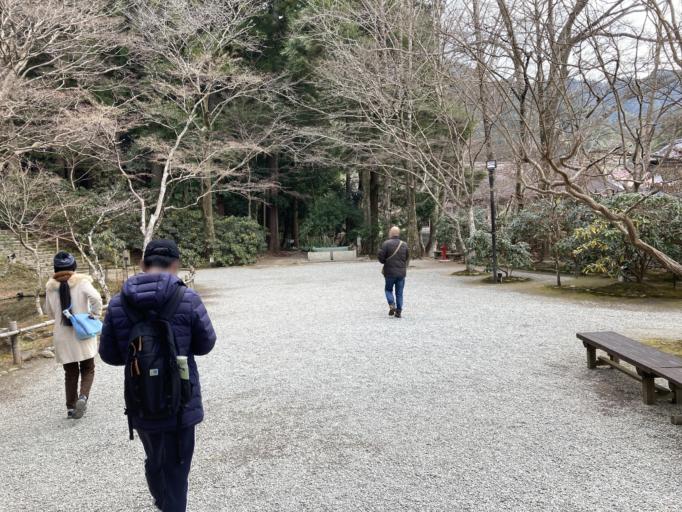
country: JP
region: Mie
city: Nabari
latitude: 34.5368
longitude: 136.0409
